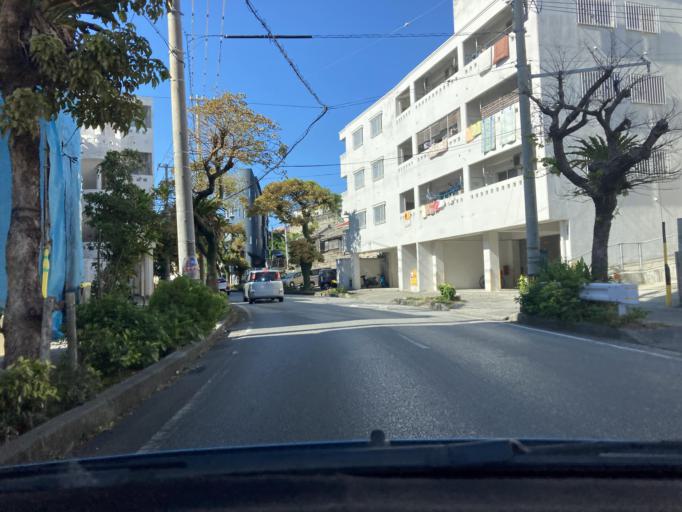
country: JP
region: Okinawa
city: Naha-shi
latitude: 26.2396
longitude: 127.6968
